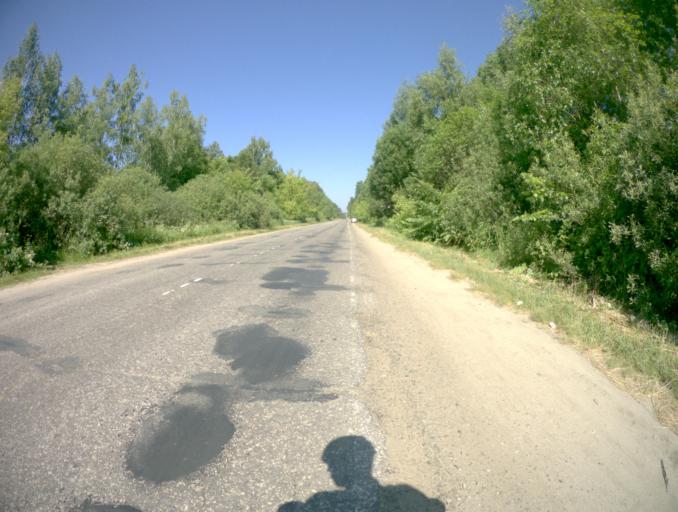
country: RU
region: Vladimir
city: Novovyazniki
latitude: 56.2278
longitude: 42.2103
